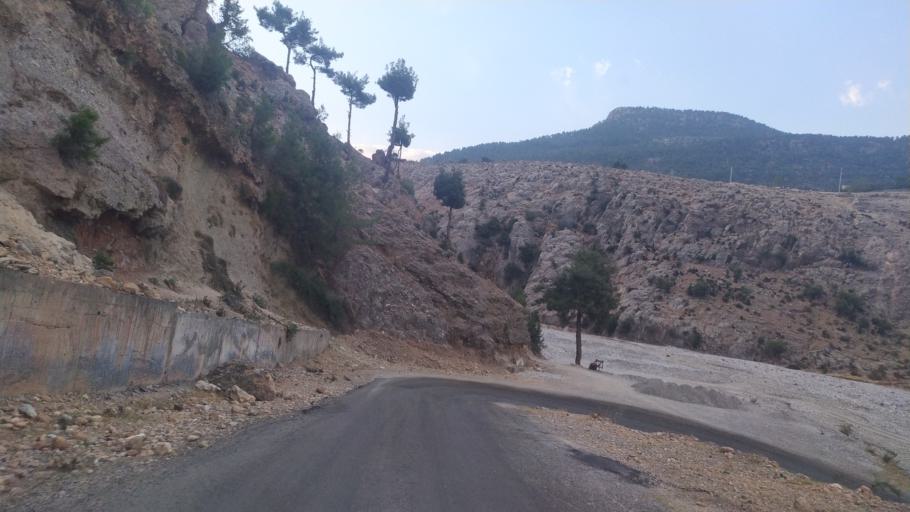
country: TR
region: Mersin
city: Camliyayla
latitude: 37.2401
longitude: 34.7126
